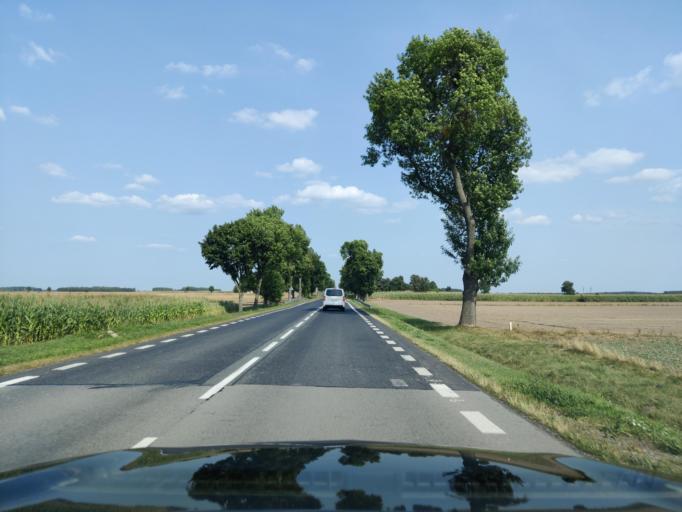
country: PL
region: Masovian Voivodeship
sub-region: Powiat makowski
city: Rzewnie
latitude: 52.8610
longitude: 21.3165
